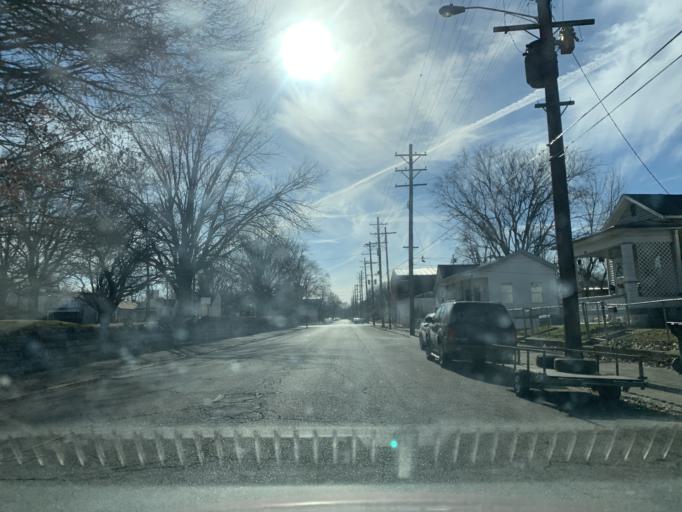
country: US
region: Kentucky
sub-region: Jefferson County
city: Louisville
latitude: 38.2619
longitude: -85.7826
